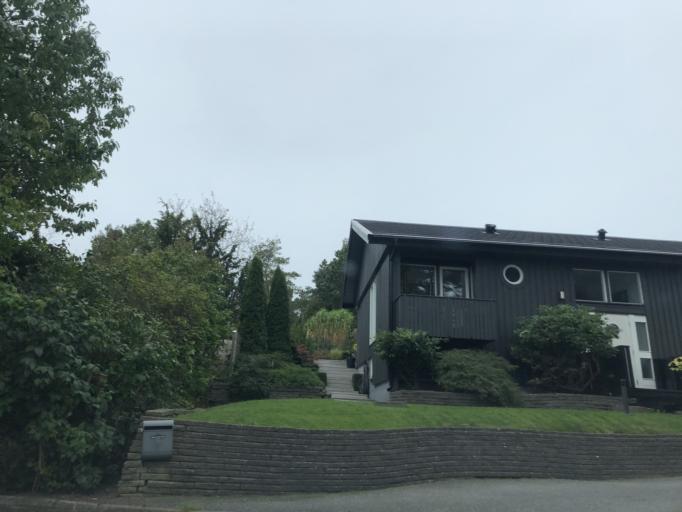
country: SE
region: Vaestra Goetaland
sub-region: Goteborg
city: Majorna
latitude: 57.6520
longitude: 11.8738
